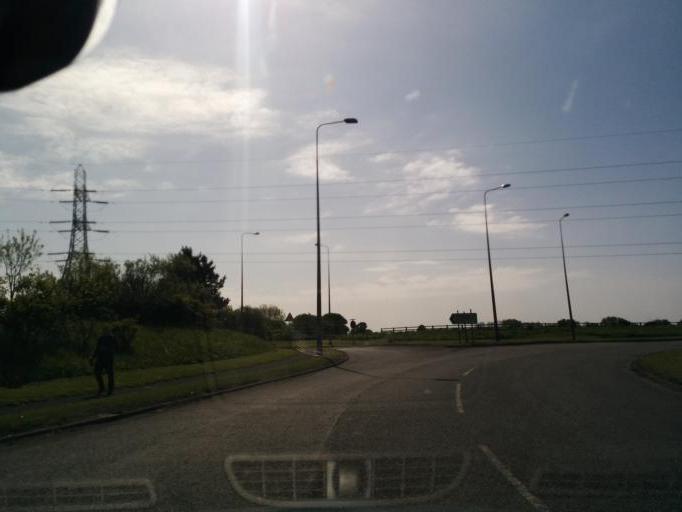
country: GB
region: England
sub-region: Northumberland
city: Newbiggin-by-the-Sea
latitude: 55.1721
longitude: -1.5313
